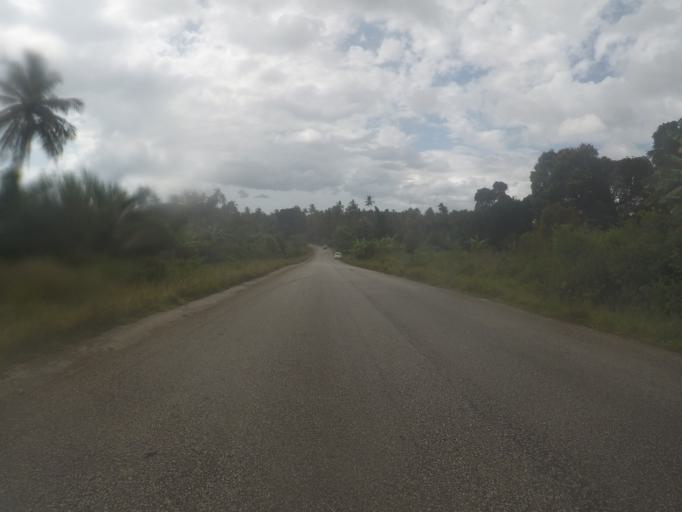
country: TZ
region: Zanzibar North
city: Mkokotoni
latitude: -5.9165
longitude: 39.2559
